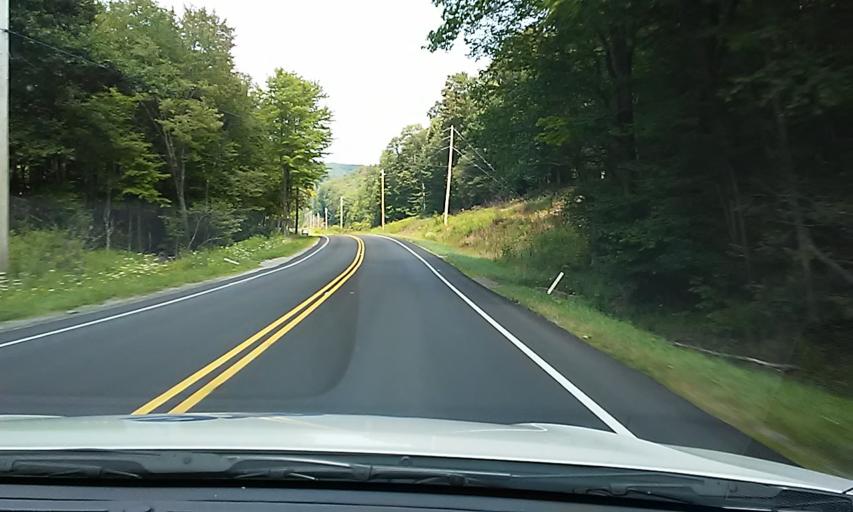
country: US
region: Pennsylvania
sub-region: Elk County
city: Saint Marys
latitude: 41.4575
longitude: -78.4305
